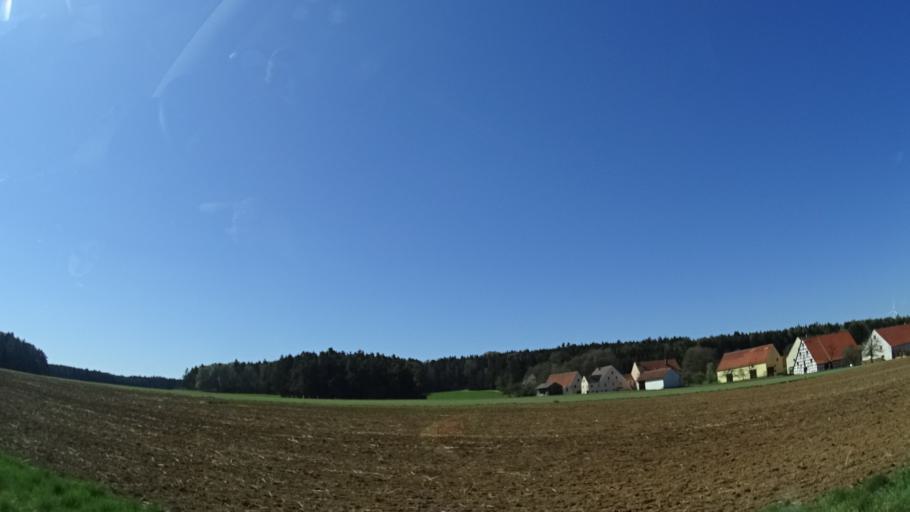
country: DE
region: Bavaria
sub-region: Regierungsbezirk Mittelfranken
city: Alfeld
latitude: 49.4215
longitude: 11.5548
